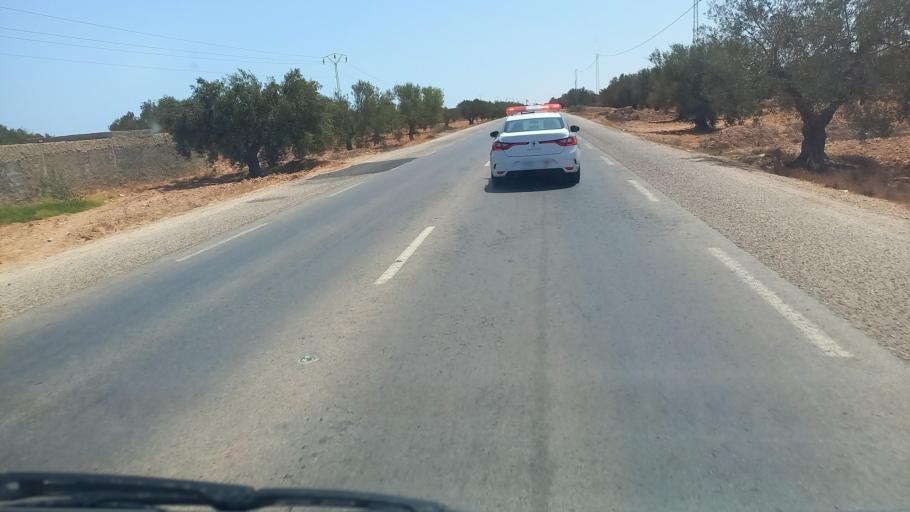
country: TN
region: Madanin
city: Zarzis
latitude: 33.5615
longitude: 11.0538
